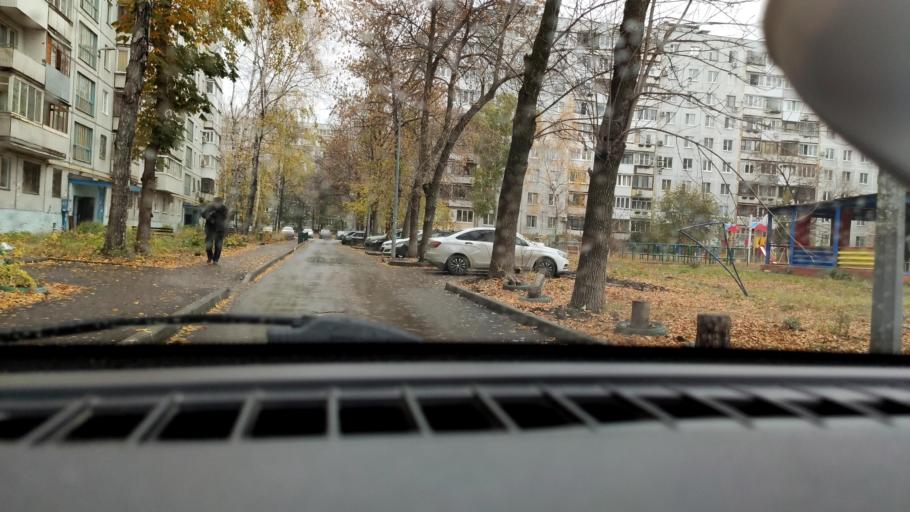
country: RU
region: Samara
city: Samara
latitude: 53.2344
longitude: 50.2111
